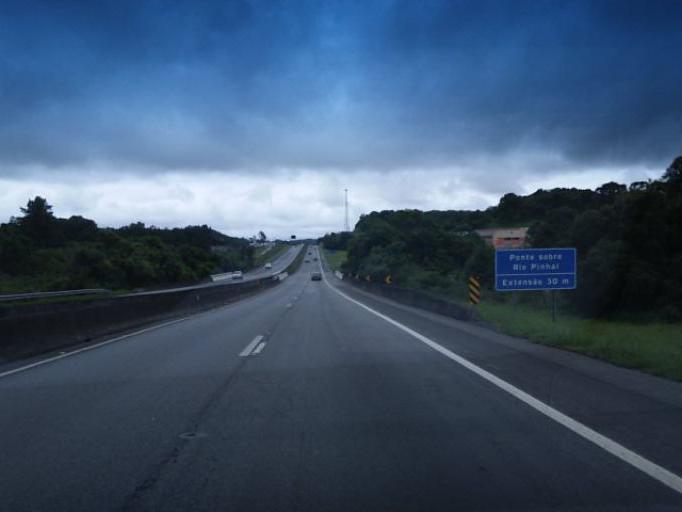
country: BR
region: Parana
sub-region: Campina Grande Do Sul
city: Campina Grande do Sul
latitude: -25.3341
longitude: -49.0339
